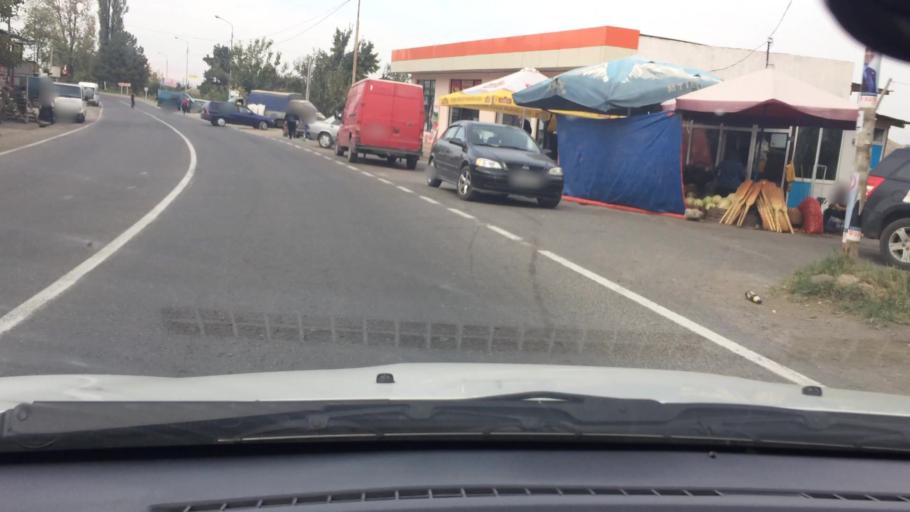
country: GE
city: Naghvarevi
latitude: 41.3658
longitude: 44.8402
